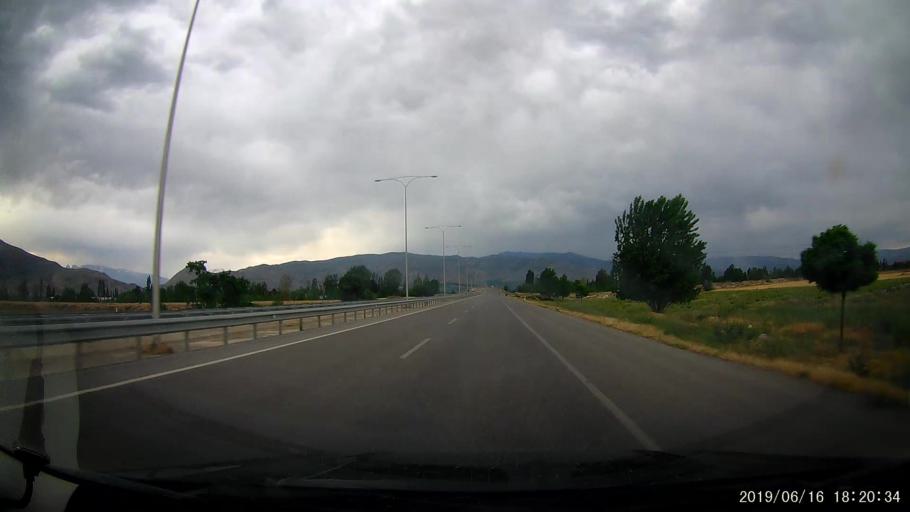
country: TR
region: Erzincan
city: Erzincan
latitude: 39.7197
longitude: 39.4659
